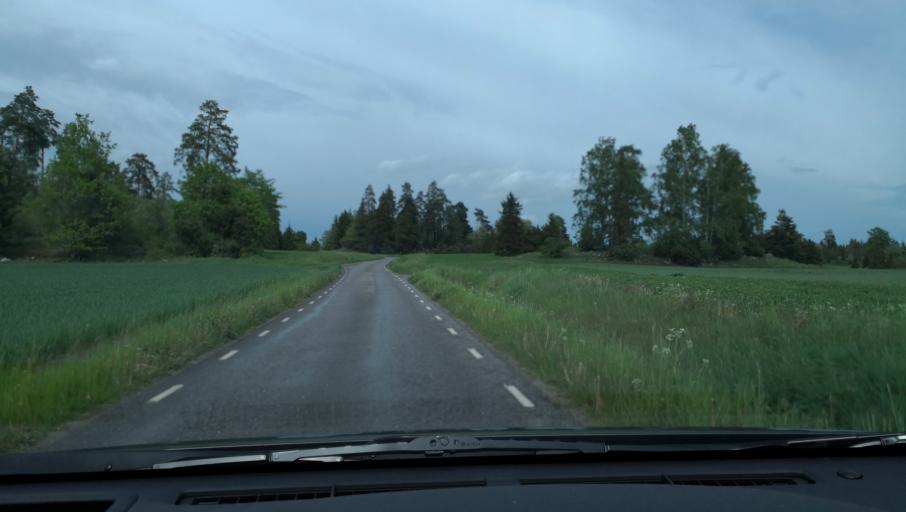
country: SE
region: Uppsala
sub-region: Enkopings Kommun
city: Orsundsbro
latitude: 59.7053
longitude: 17.4204
